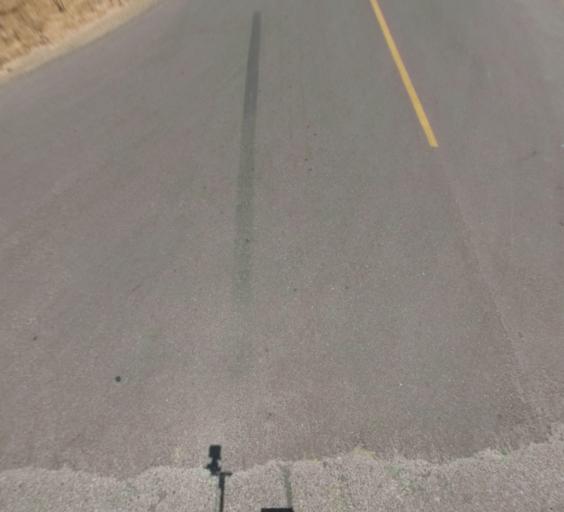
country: US
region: California
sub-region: Madera County
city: Madera Acres
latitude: 37.0396
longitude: -119.9927
